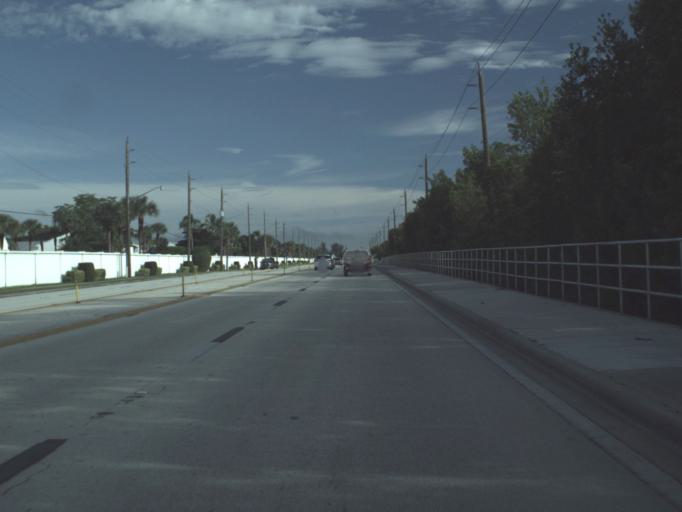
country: US
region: Florida
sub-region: Lee County
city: Fort Myers Beach
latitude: 26.4728
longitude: -81.9510
